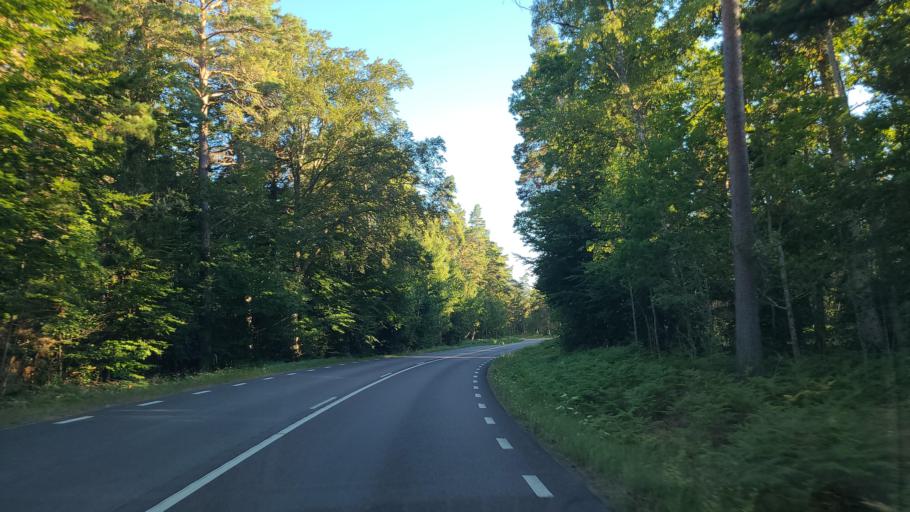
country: SE
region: Kalmar
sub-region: Borgholms Kommun
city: Borgholm
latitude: 57.2939
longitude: 17.0206
